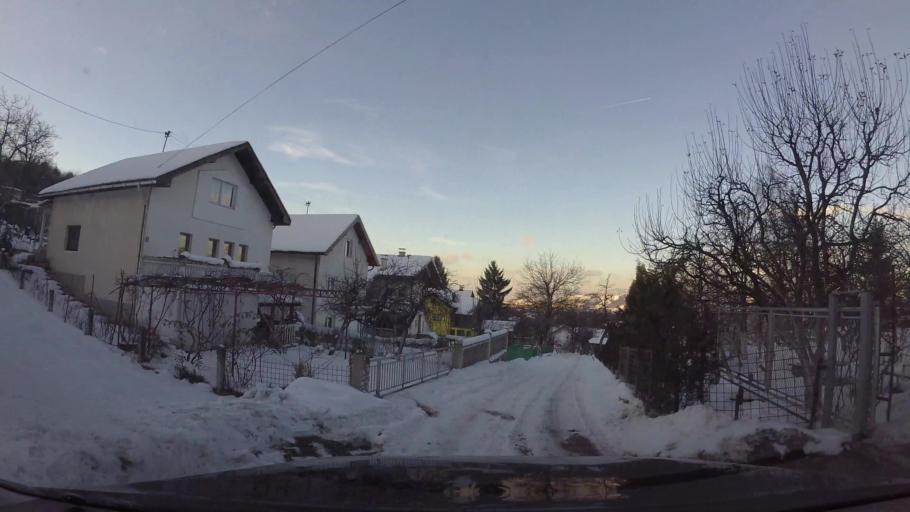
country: BA
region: Federation of Bosnia and Herzegovina
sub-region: Kanton Sarajevo
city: Sarajevo
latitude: 43.8063
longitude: 18.3582
